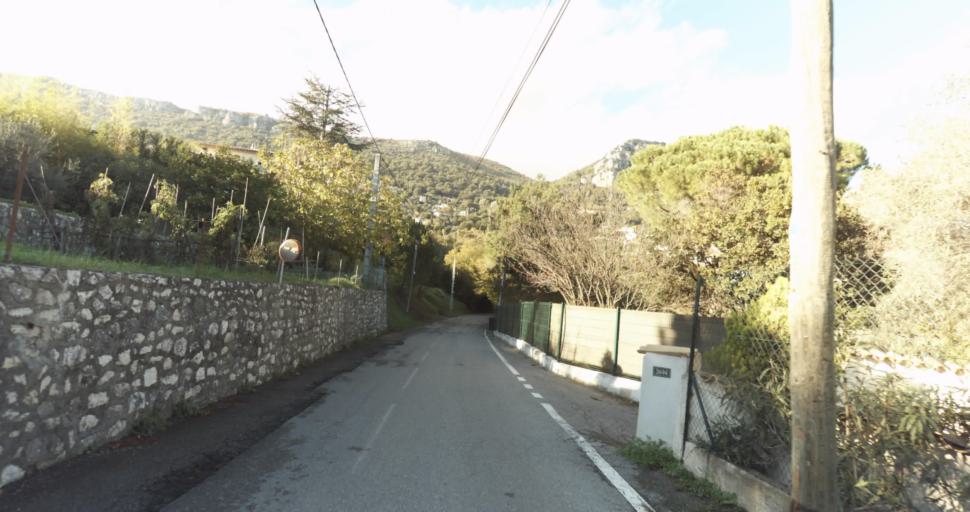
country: FR
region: Provence-Alpes-Cote d'Azur
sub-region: Departement des Alpes-Maritimes
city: Vence
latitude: 43.7324
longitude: 7.1279
